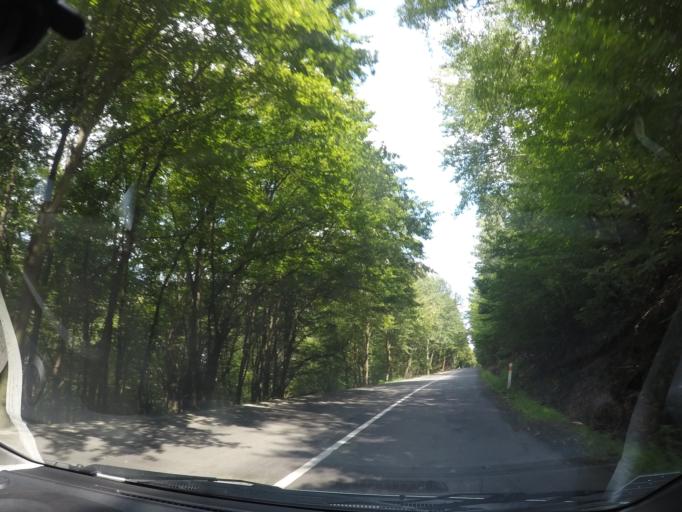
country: SK
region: Banskobystricky
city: Dudince
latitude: 48.2620
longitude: 18.8665
